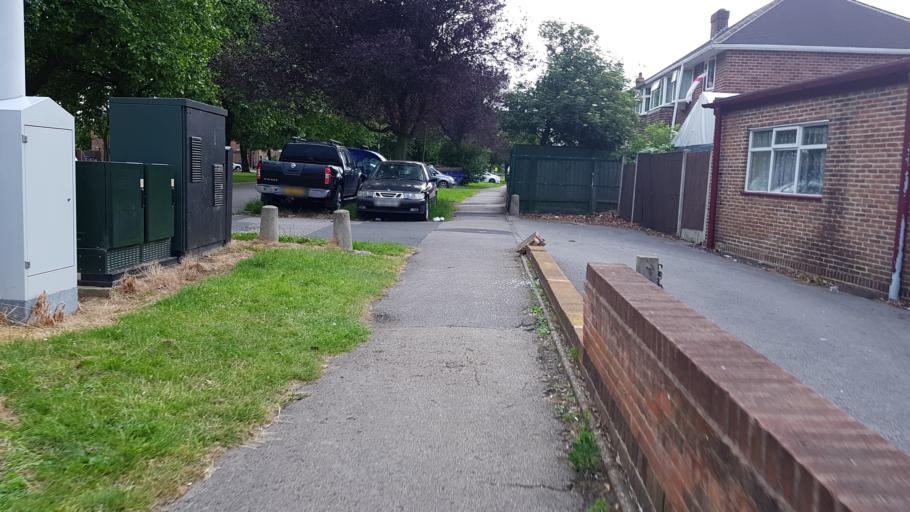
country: GB
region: England
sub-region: Derby
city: Derby
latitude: 52.8886
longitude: -1.4370
